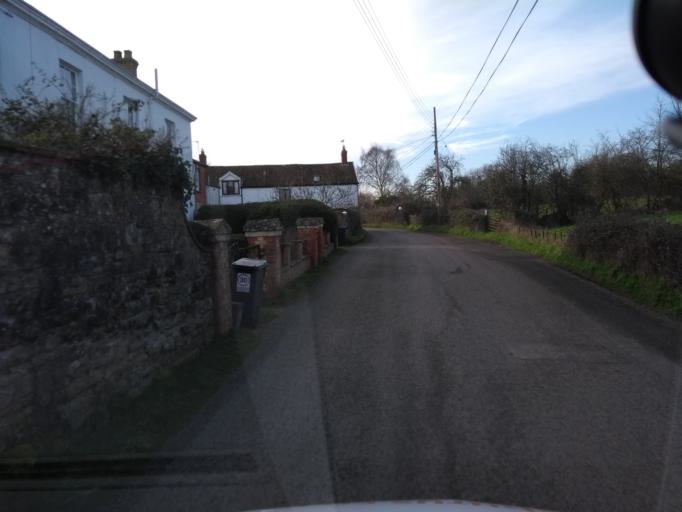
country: GB
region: England
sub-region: Somerset
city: Creech Saint Michael
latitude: 51.0171
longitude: -2.9748
